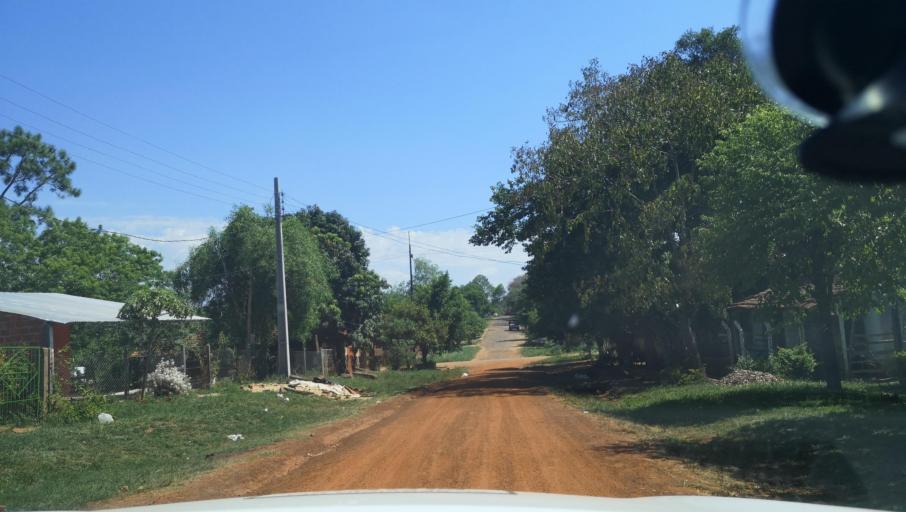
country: PY
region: Itapua
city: Carmen del Parana
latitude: -27.1721
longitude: -56.2474
